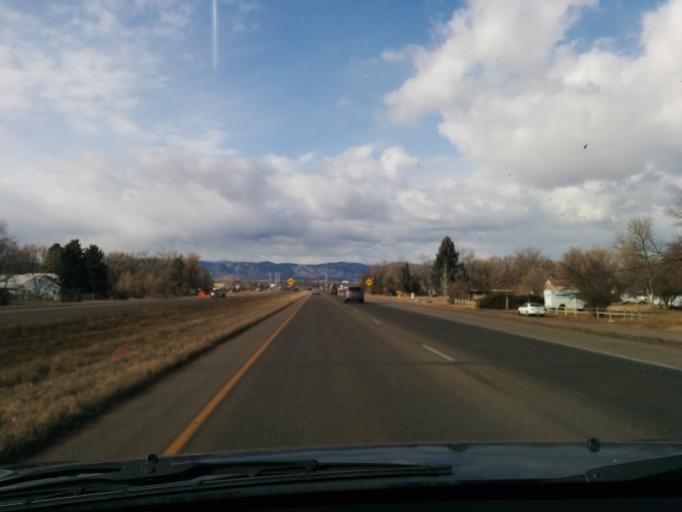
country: US
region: Colorado
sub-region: Larimer County
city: Fort Collins
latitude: 40.5814
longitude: -105.0223
